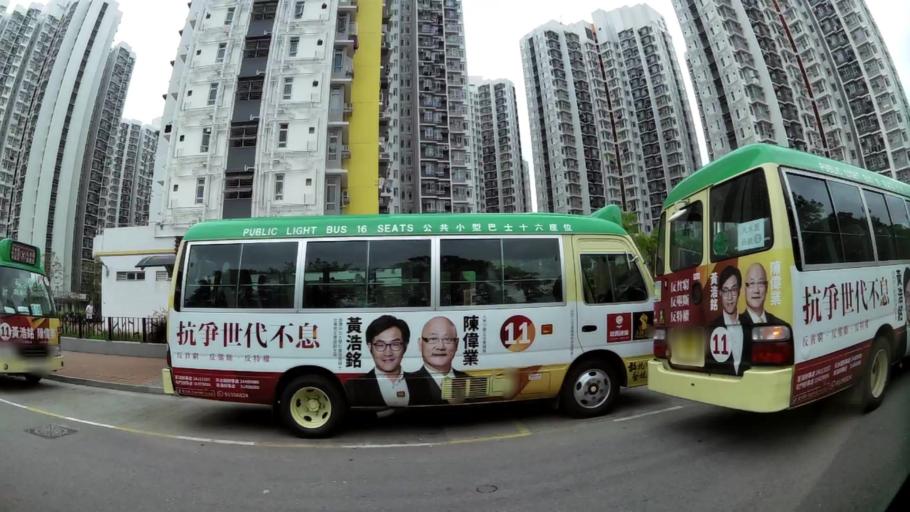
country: HK
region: Yuen Long
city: Yuen Long Kau Hui
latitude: 22.4369
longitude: 113.9968
